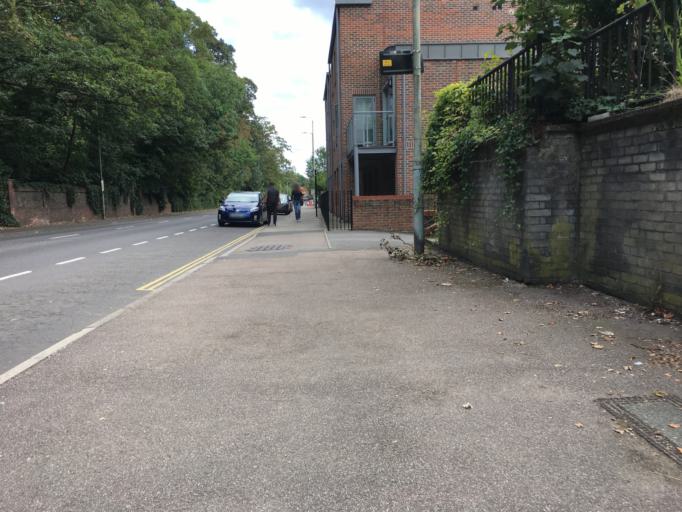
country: GB
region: England
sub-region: Hertfordshire
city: St Albans
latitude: 51.7469
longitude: -0.3302
